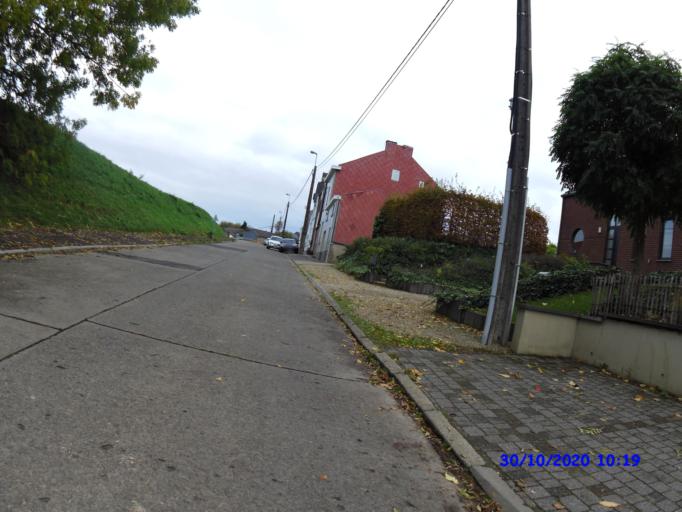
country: BE
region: Wallonia
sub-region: Province de Liege
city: Berloz
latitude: 50.7136
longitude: 5.2148
